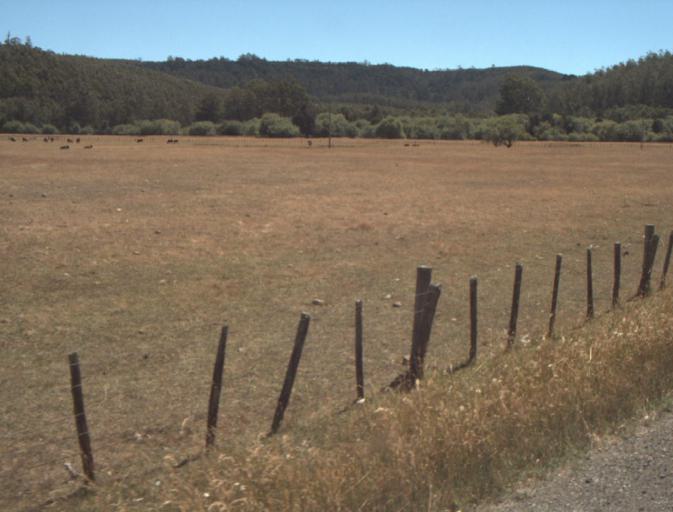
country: AU
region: Tasmania
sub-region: Dorset
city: Scottsdale
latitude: -41.2894
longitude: 147.3847
